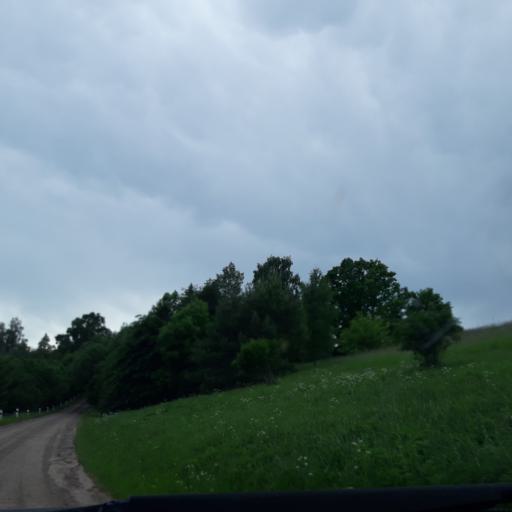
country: LV
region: Talsu Rajons
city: Sabile
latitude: 57.0233
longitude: 22.5910
